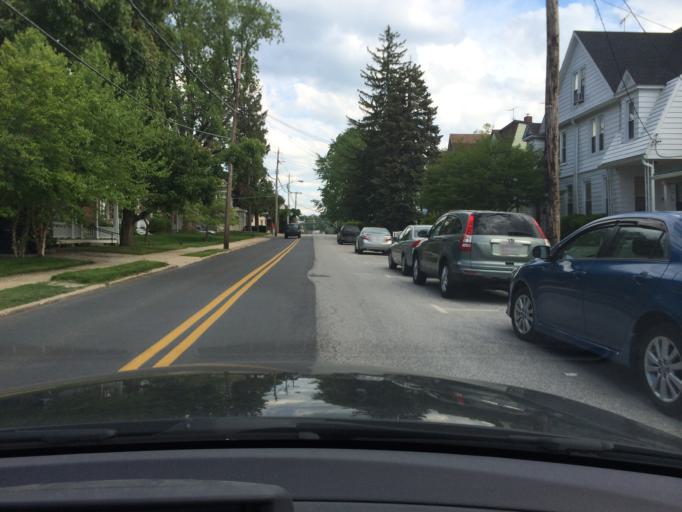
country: US
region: Maryland
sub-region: Carroll County
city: Westminster
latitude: 39.5715
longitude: -76.9943
